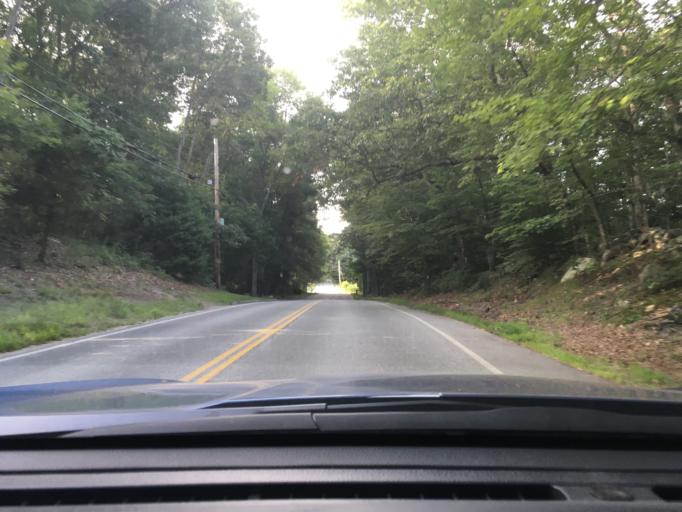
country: US
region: Rhode Island
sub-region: Kent County
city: West Warwick
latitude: 41.6375
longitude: -71.5147
